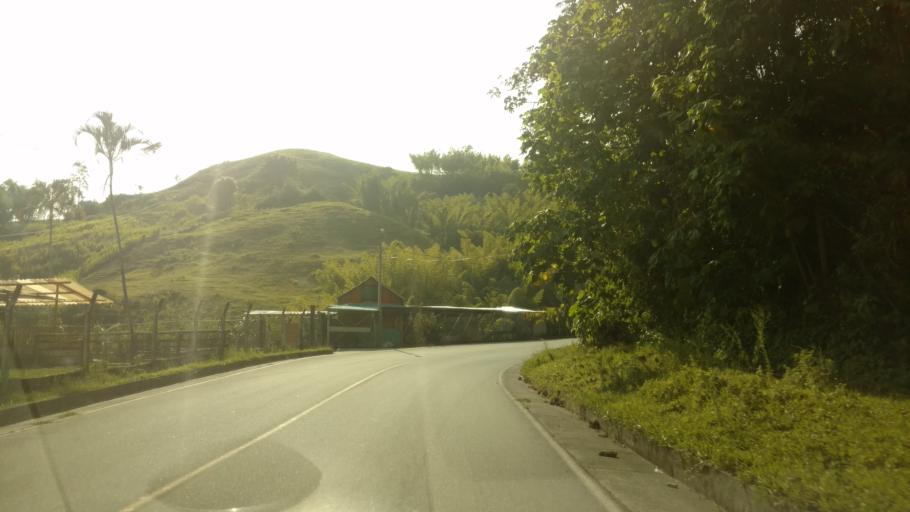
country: CO
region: Caldas
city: Neira
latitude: 5.1439
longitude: -75.5050
